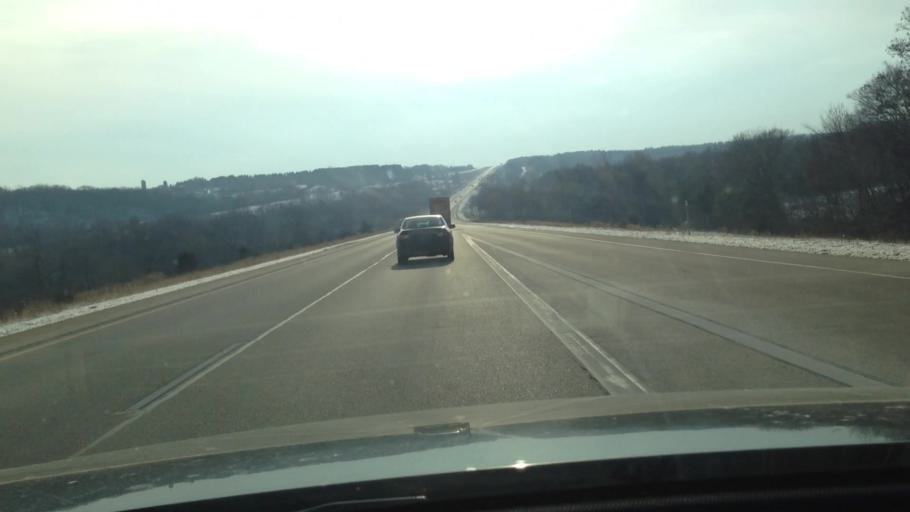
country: US
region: Wisconsin
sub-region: Walworth County
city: East Troy
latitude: 42.7293
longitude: -88.4631
